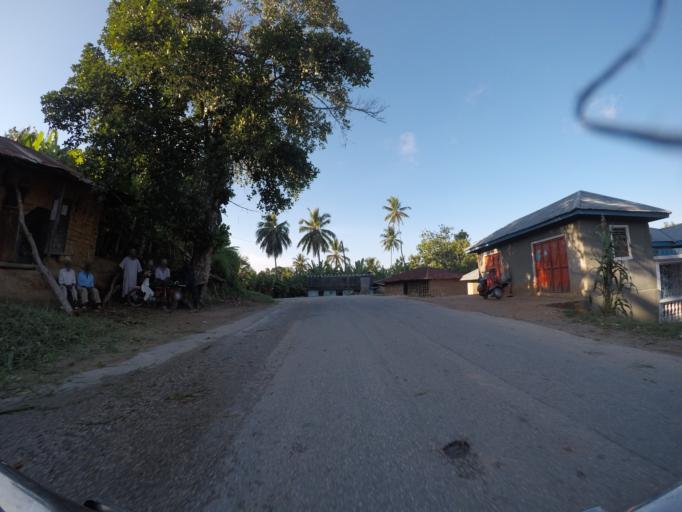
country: TZ
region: Pemba South
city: Mtambile
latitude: -5.3791
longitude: 39.6941
